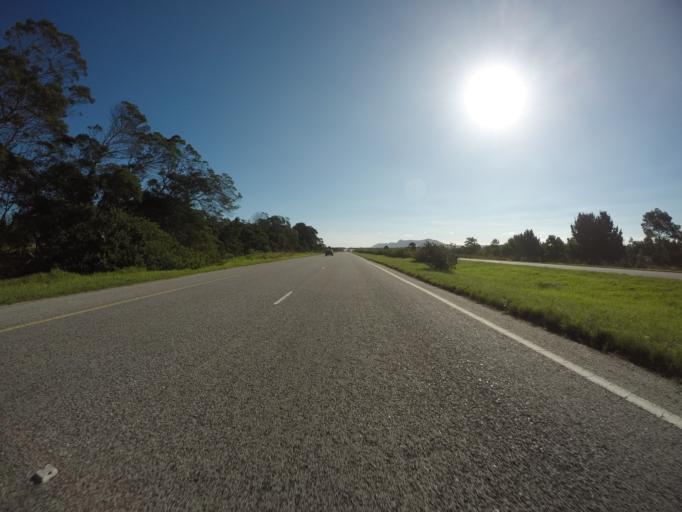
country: ZA
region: Eastern Cape
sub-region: Nelson Mandela Bay Metropolitan Municipality
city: Uitenhage
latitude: -33.9348
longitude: 25.3609
